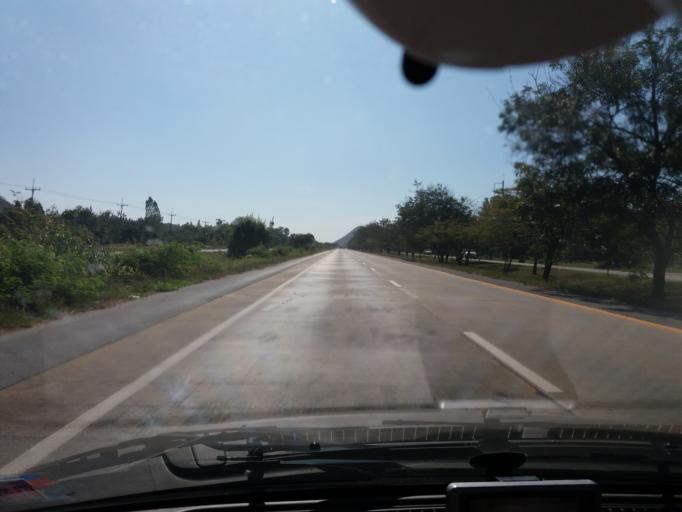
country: TH
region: Suphan Buri
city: Doem Bang Nang Buat
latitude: 14.8625
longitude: 100.0904
